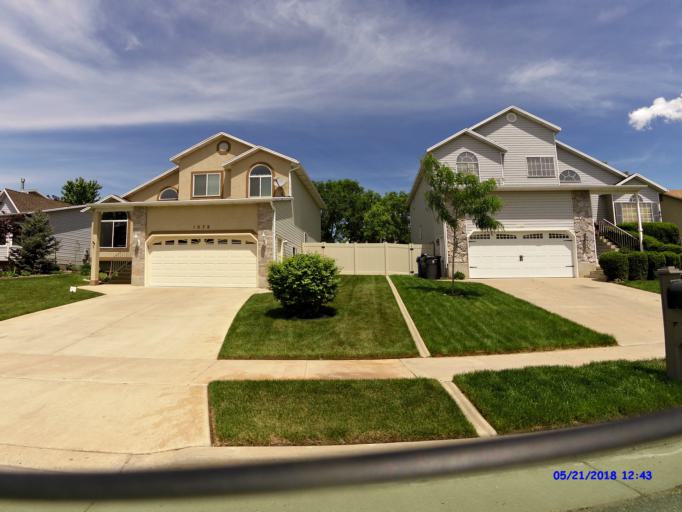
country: US
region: Utah
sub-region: Weber County
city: Washington Terrace
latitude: 41.1721
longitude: -111.9523
